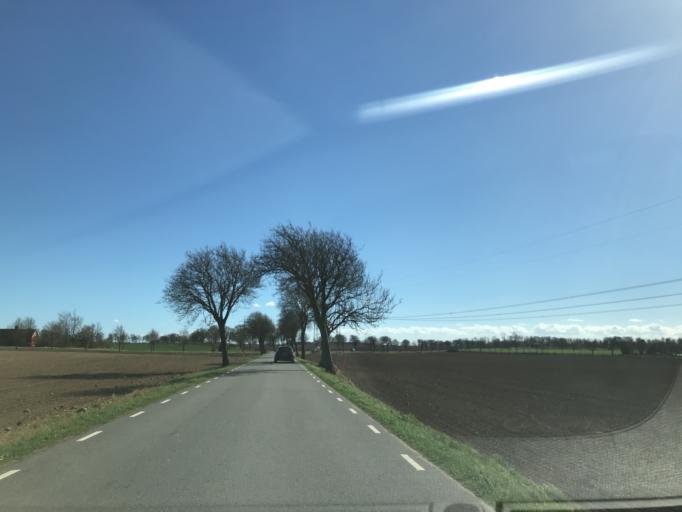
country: SE
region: Skane
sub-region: Svalovs Kommun
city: Svaloev
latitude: 55.9485
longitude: 13.0305
